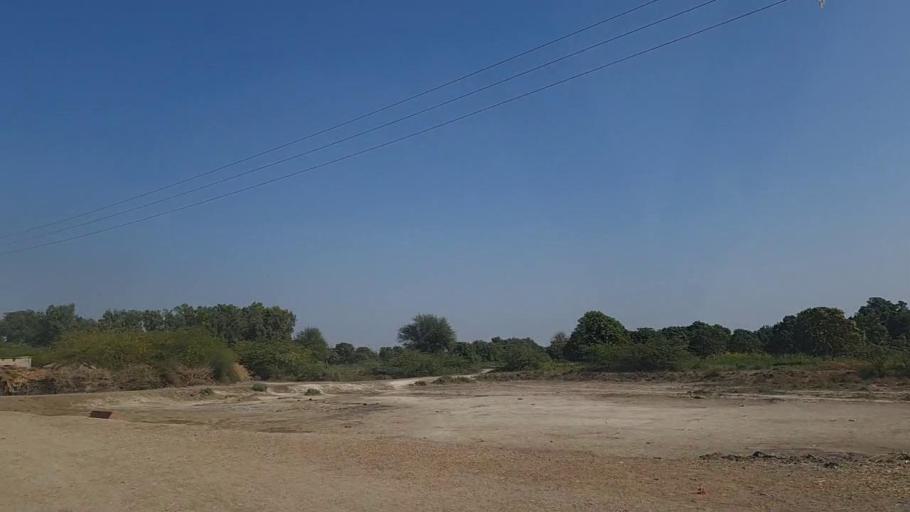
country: PK
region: Sindh
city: Digri
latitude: 25.1576
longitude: 69.1422
